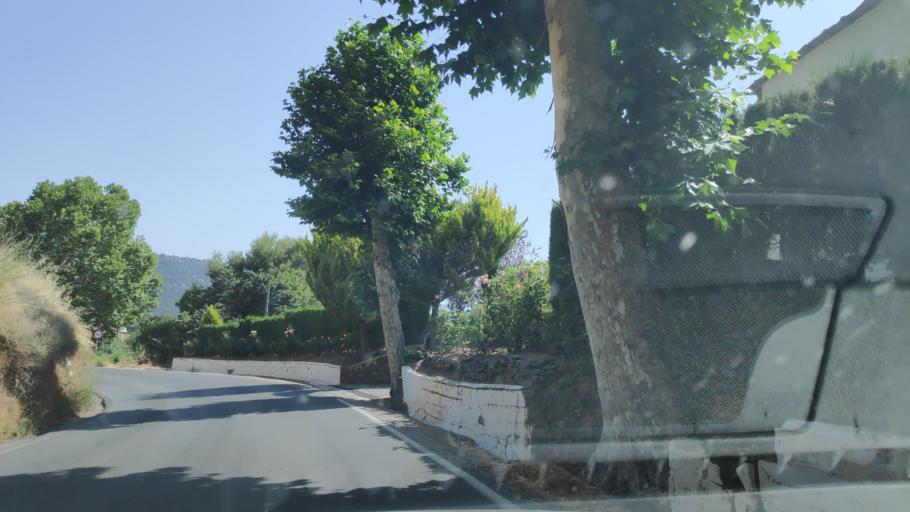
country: ES
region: Andalusia
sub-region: Provincia de Granada
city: Bubion
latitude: 36.9544
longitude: -3.3553
